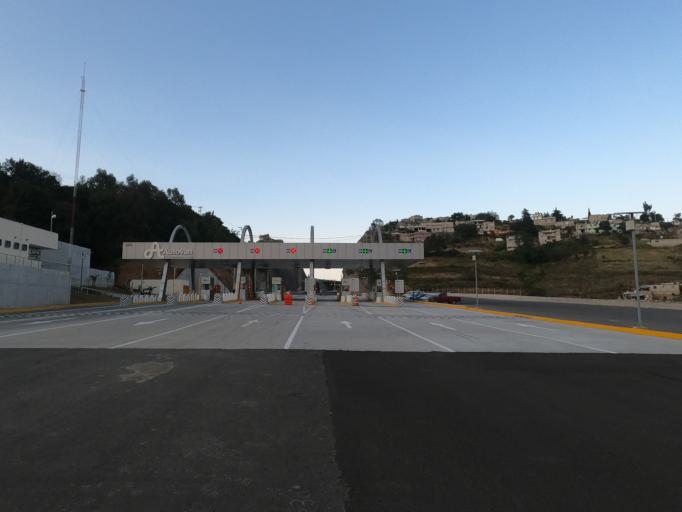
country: MX
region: Mexico
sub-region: Naucalpan de Juarez
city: Ejido el Castillo
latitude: 19.4338
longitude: -99.3037
